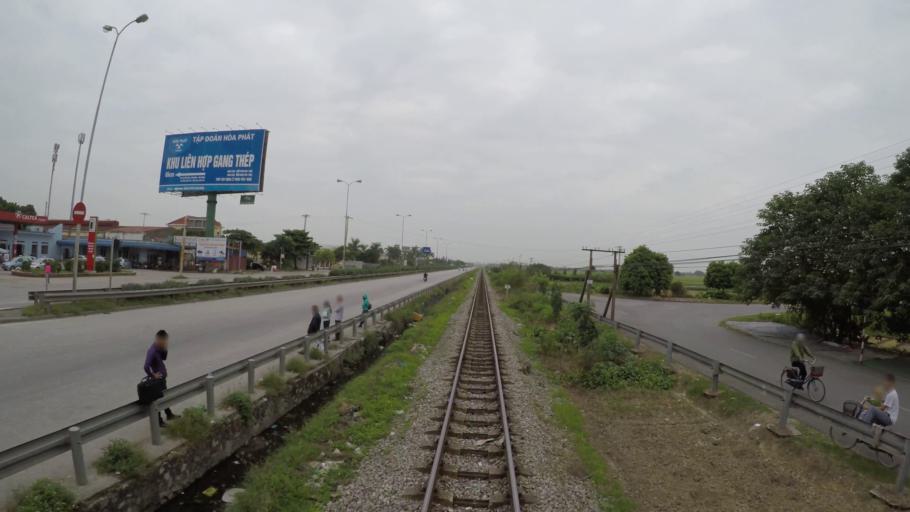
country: VN
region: Hai Duong
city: Phu Thai
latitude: 20.9658
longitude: 106.5115
